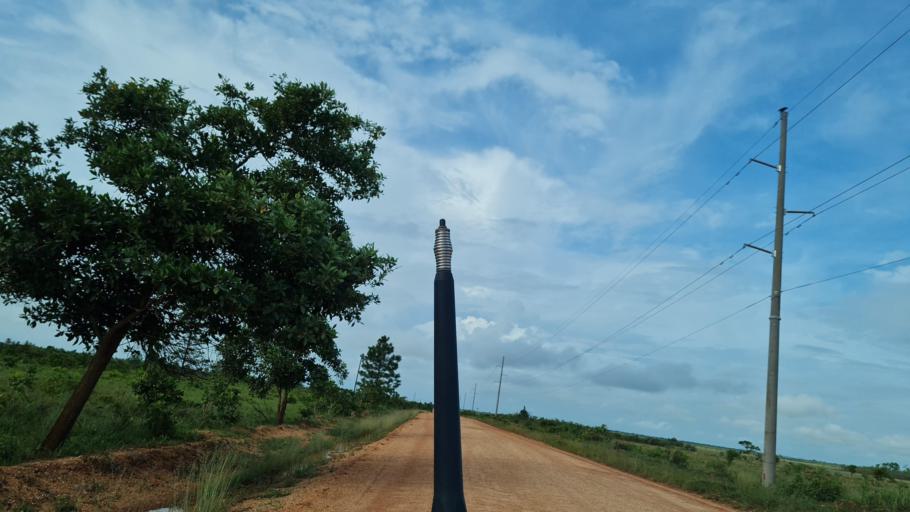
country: NI
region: Atlantico Norte (RAAN)
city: Puerto Cabezas
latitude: 14.1514
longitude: -83.5322
